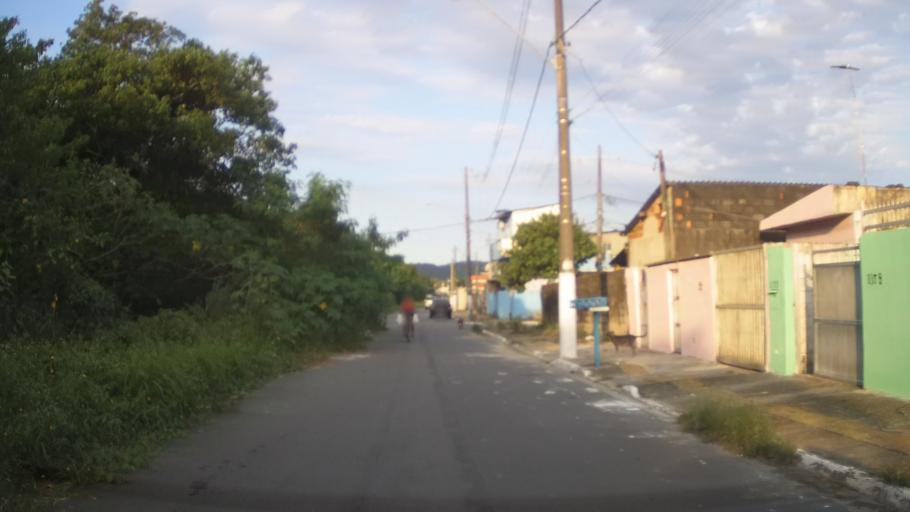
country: BR
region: Sao Paulo
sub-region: Praia Grande
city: Praia Grande
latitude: -23.9940
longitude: -46.4251
